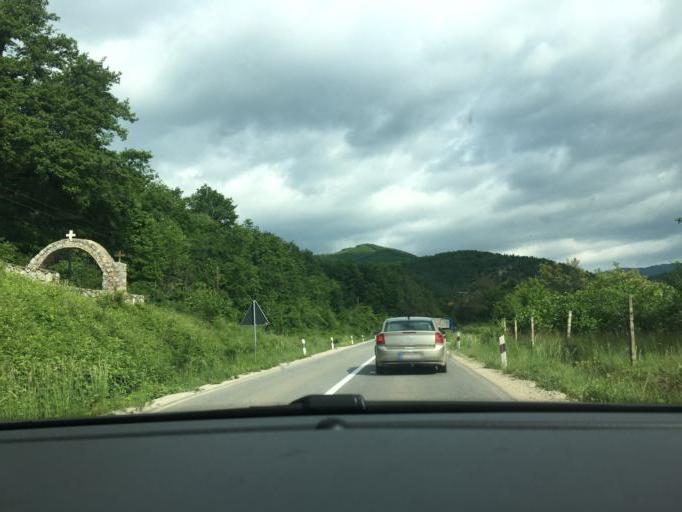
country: MK
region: Resen
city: Jankovec
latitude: 41.1279
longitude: 21.0061
